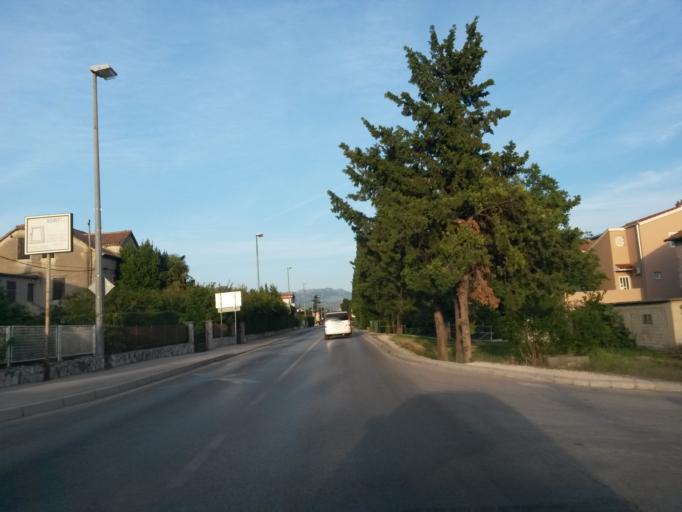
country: HR
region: Splitsko-Dalmatinska
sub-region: Grad Split
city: Split
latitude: 43.5535
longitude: 16.3664
